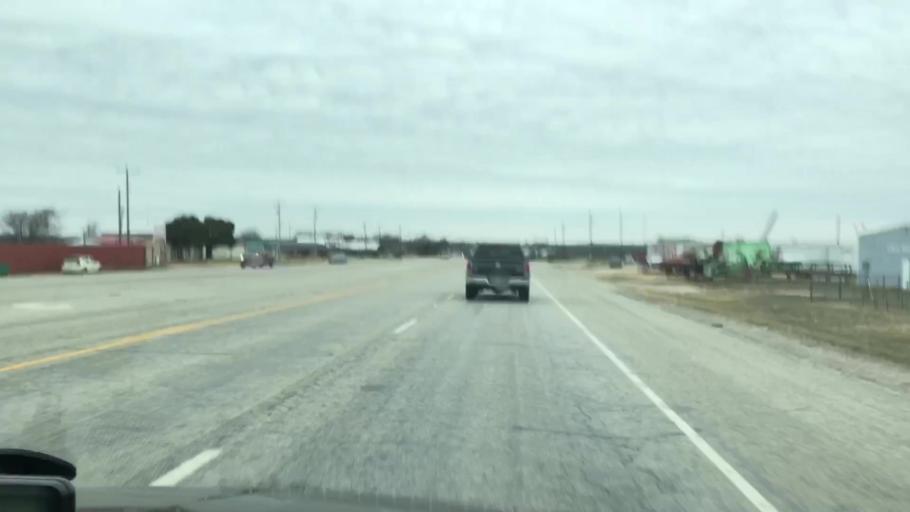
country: US
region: Texas
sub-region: Jack County
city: Jacksboro
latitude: 33.2024
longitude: -98.1507
